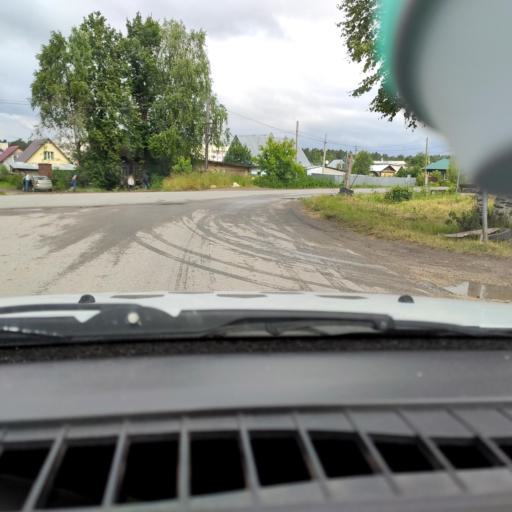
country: RU
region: Perm
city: Dobryanka
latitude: 58.4715
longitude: 56.4110
